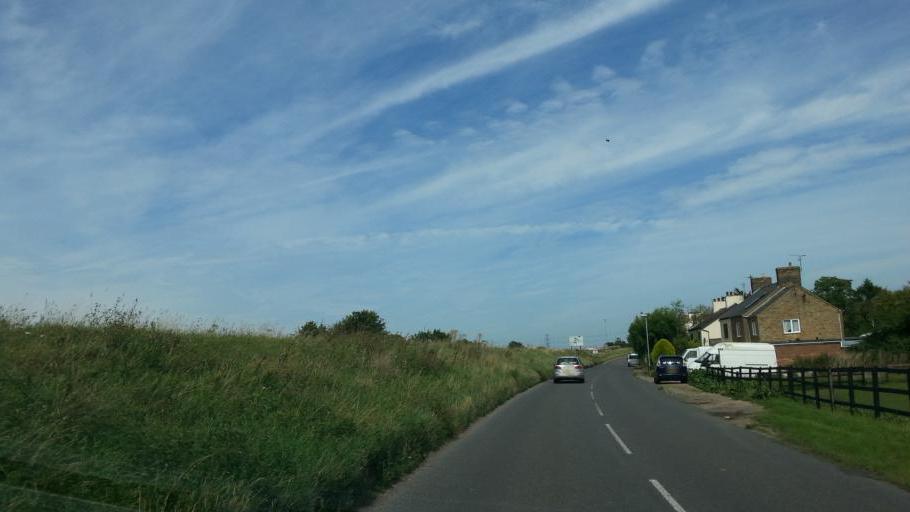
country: GB
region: England
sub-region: Cambridgeshire
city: Littleport
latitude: 52.4630
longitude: 0.3200
